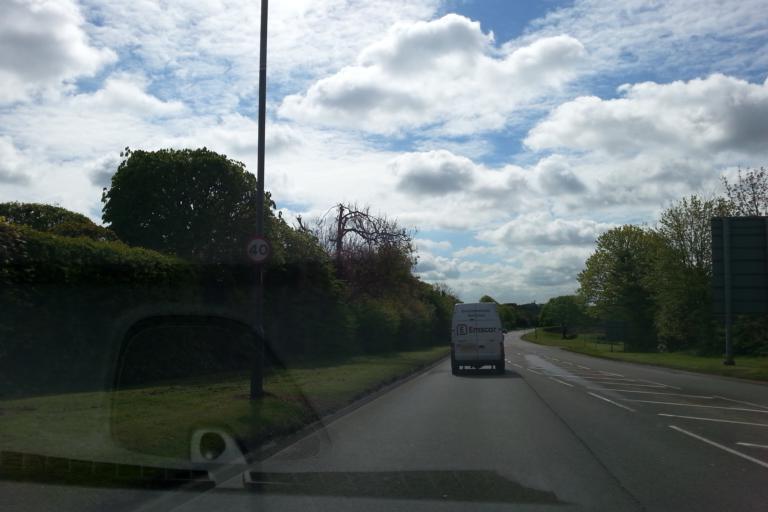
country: GB
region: England
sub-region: Staffordshire
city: Lichfield
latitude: 52.6916
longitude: -1.8480
